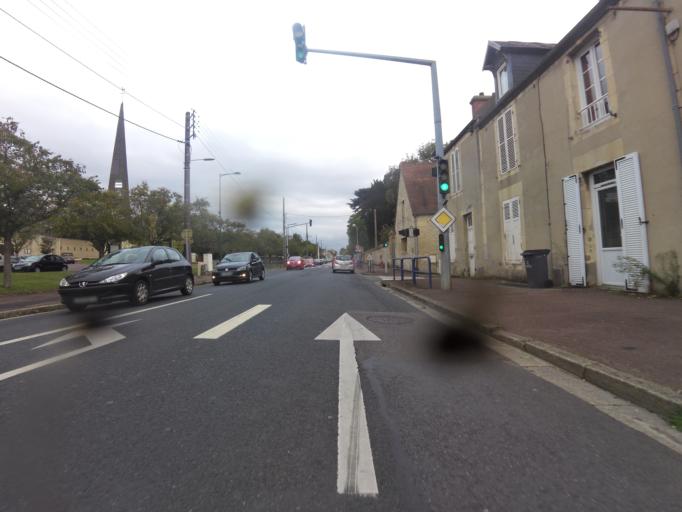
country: FR
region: Lower Normandy
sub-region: Departement du Calvados
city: Bretteville-sur-Odon
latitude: 49.1664
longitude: -0.4139
